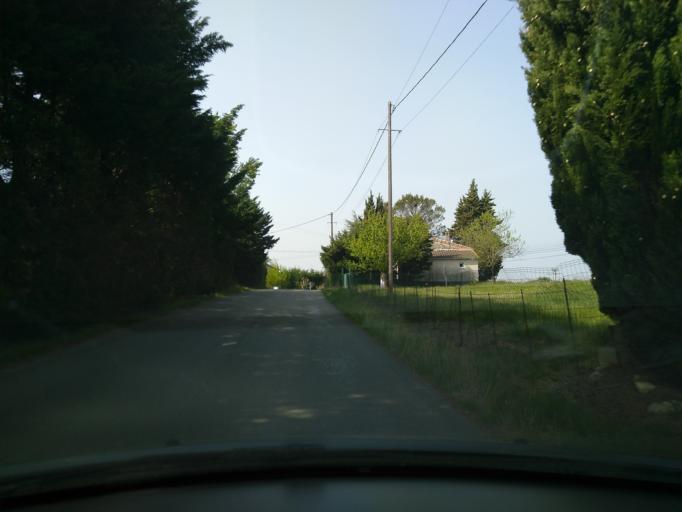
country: FR
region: Rhone-Alpes
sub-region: Departement de l'Ardeche
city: Ruoms
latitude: 44.4531
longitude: 4.3980
